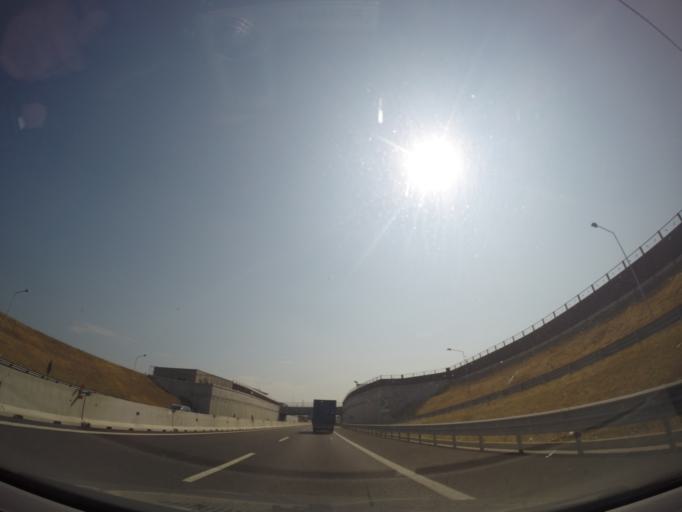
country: IT
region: Lombardy
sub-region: Provincia di Brescia
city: Ospitaletto
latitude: 45.5373
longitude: 10.0726
